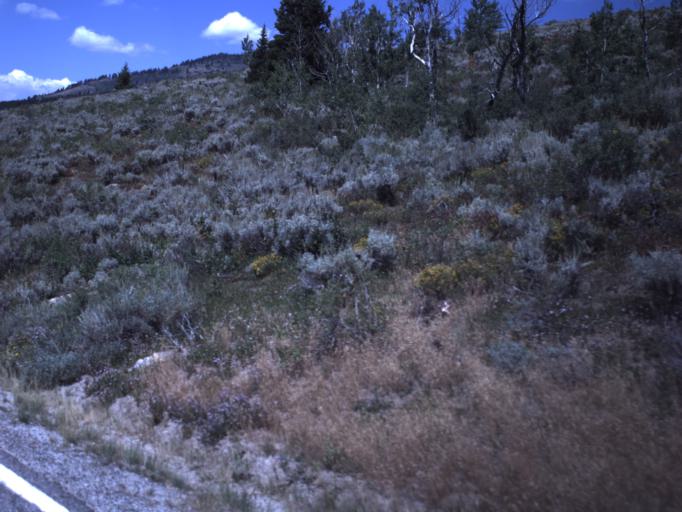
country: US
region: Idaho
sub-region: Bear Lake County
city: Paris
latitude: 41.9564
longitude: -111.4996
